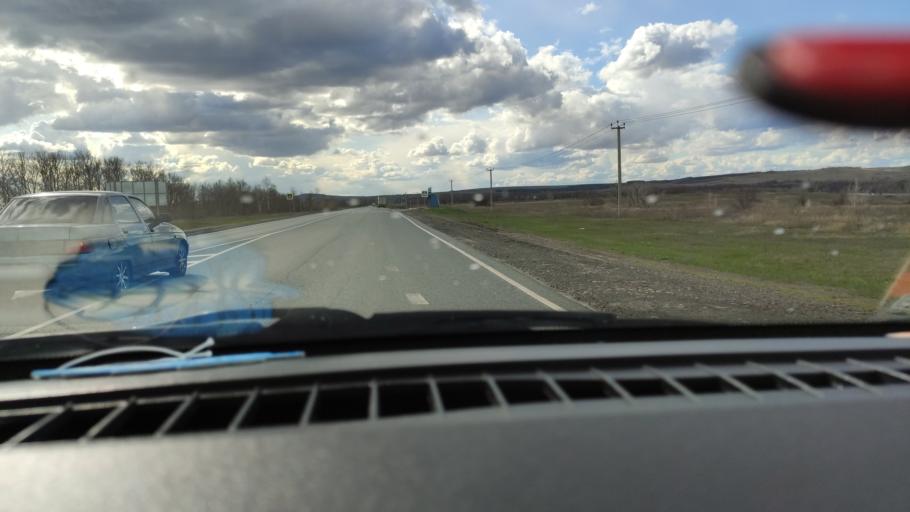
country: RU
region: Saratov
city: Tersa
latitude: 52.0852
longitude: 47.6264
